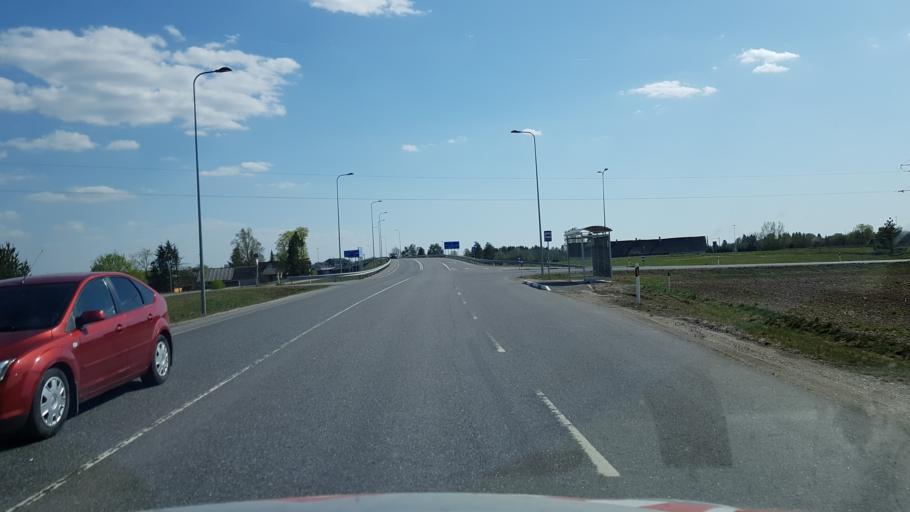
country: EE
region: Harju
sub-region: Raasiku vald
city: Arukula
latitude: 59.1857
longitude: 25.1157
